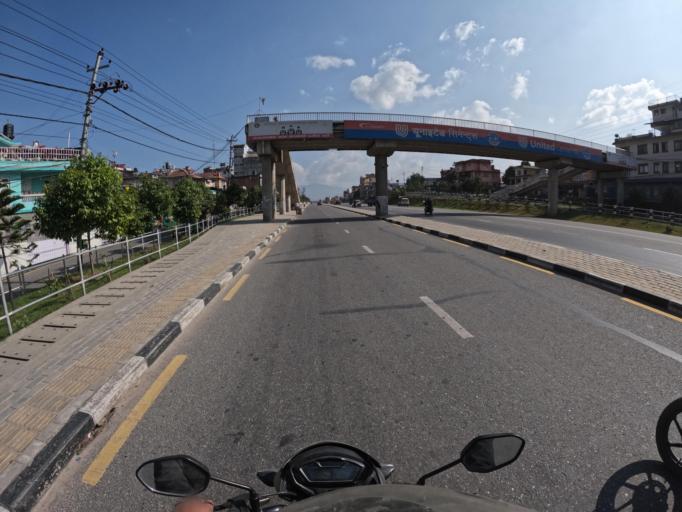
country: NP
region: Central Region
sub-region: Bagmati Zone
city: Patan
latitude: 27.6729
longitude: 85.3034
